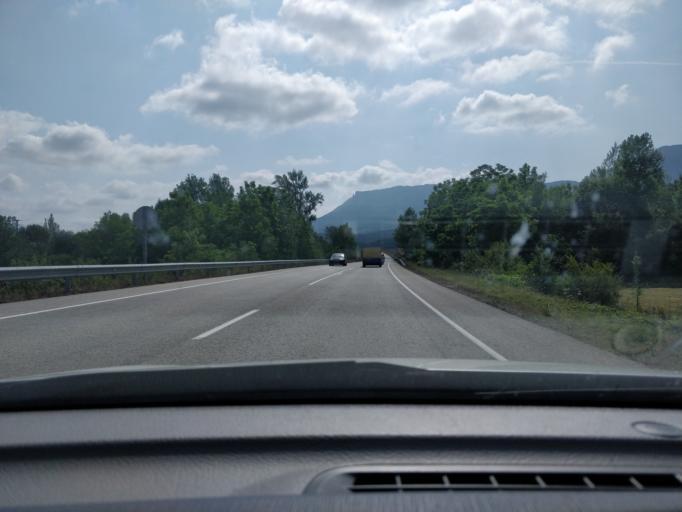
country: ES
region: Castille and Leon
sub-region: Provincia de Burgos
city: Villasana de Mena
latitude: 43.0945
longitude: -3.2986
